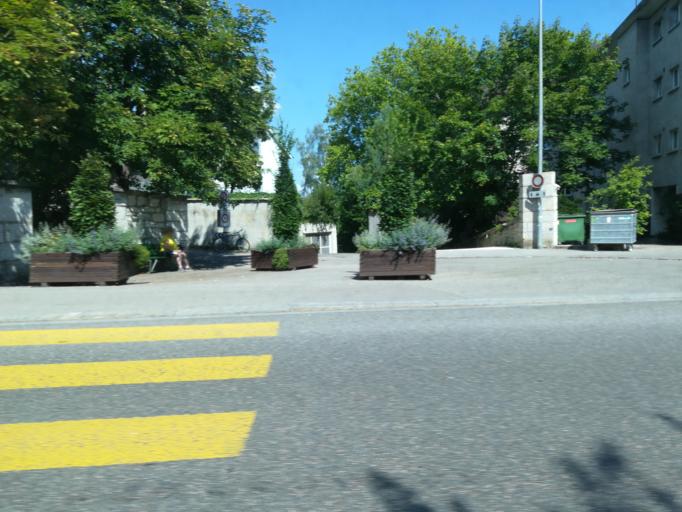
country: CH
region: Schaffhausen
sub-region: Bezirk Schaffhausen
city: Schaffhausen
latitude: 47.6988
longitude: 8.6275
